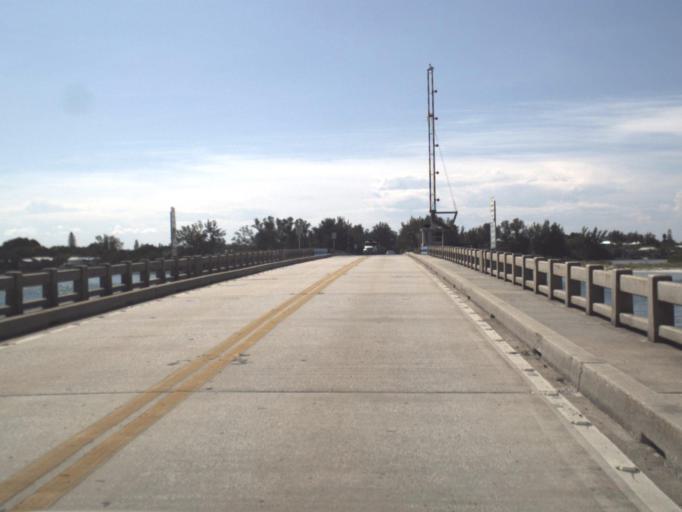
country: US
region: Florida
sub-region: Manatee County
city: Cortez
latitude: 27.4451
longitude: -82.6884
